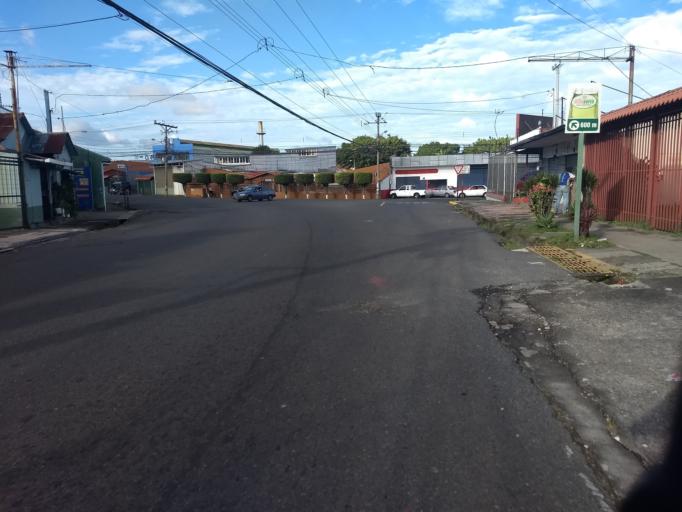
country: CR
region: San Jose
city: Colima
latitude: 9.9556
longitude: -84.0850
